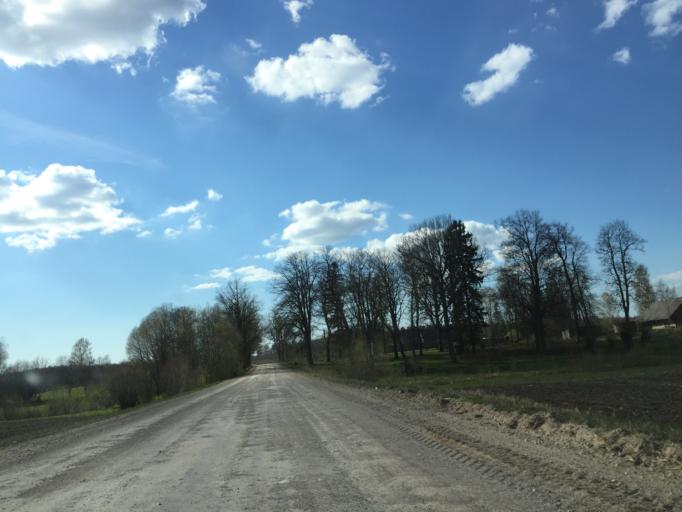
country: LV
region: Krimulda
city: Ragana
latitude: 57.3403
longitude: 24.6194
